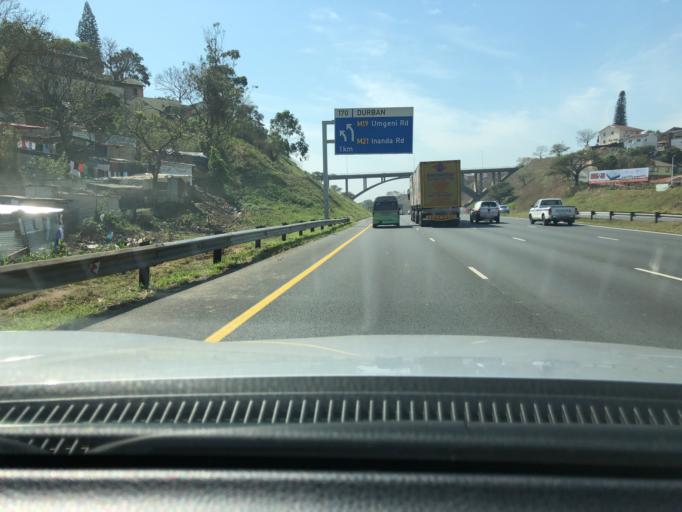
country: ZA
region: KwaZulu-Natal
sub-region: eThekwini Metropolitan Municipality
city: Berea
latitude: -29.8195
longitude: 30.9689
